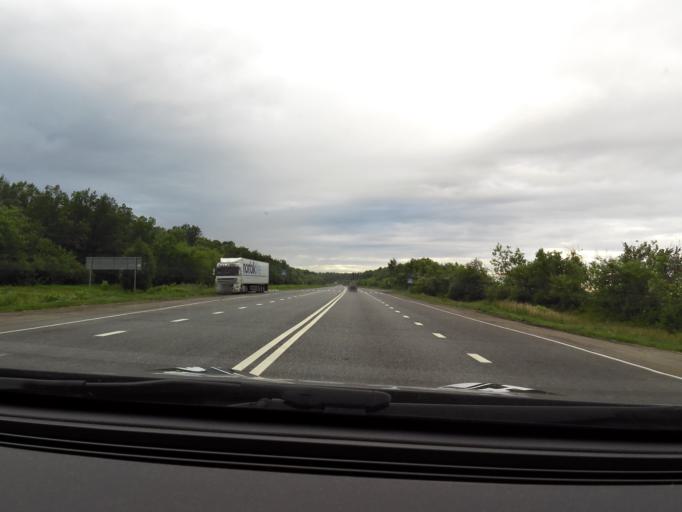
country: RU
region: Chuvashia
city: Kozlovka
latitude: 55.7939
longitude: 48.1344
